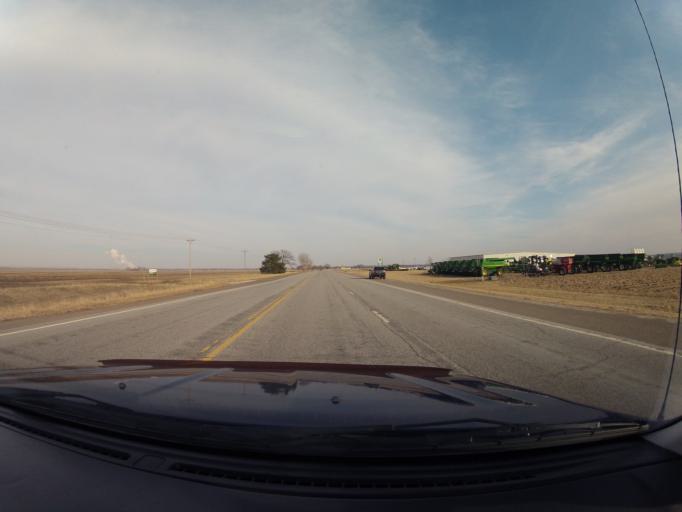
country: US
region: Kansas
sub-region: Pottawatomie County
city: Wamego
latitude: 39.2099
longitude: -96.2865
